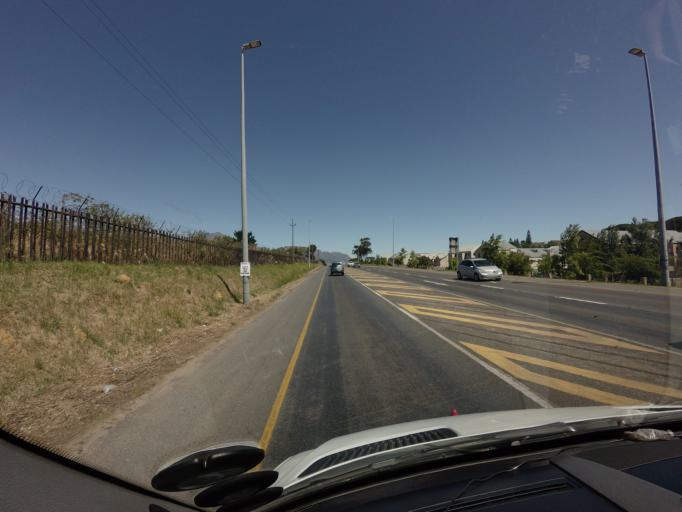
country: ZA
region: Western Cape
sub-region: Cape Winelands District Municipality
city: Stellenbosch
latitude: -33.9004
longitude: 18.8589
